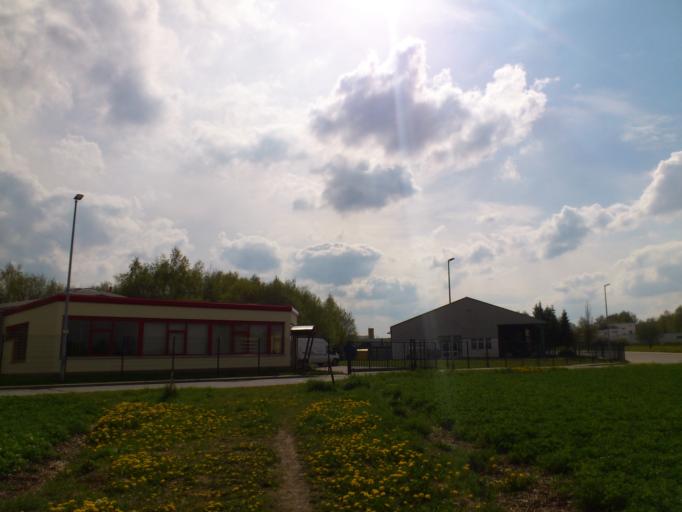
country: DE
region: Saxony
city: Neukirchen
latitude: 50.7748
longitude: 12.8703
